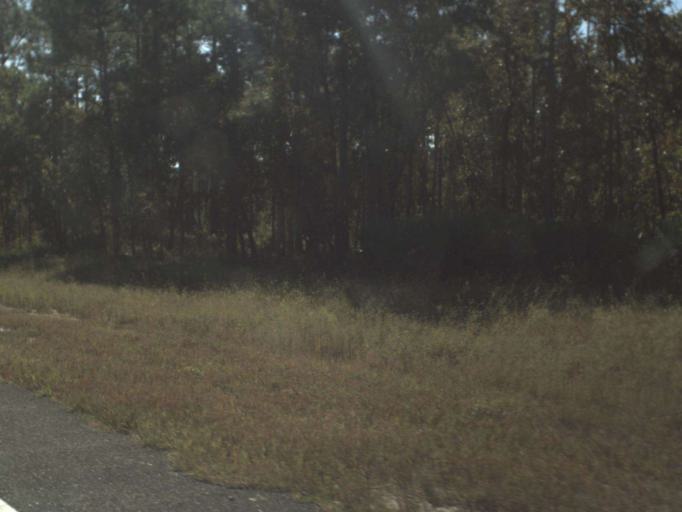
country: US
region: Florida
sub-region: Wakulla County
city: Crawfordville
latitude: 30.2994
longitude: -84.4161
